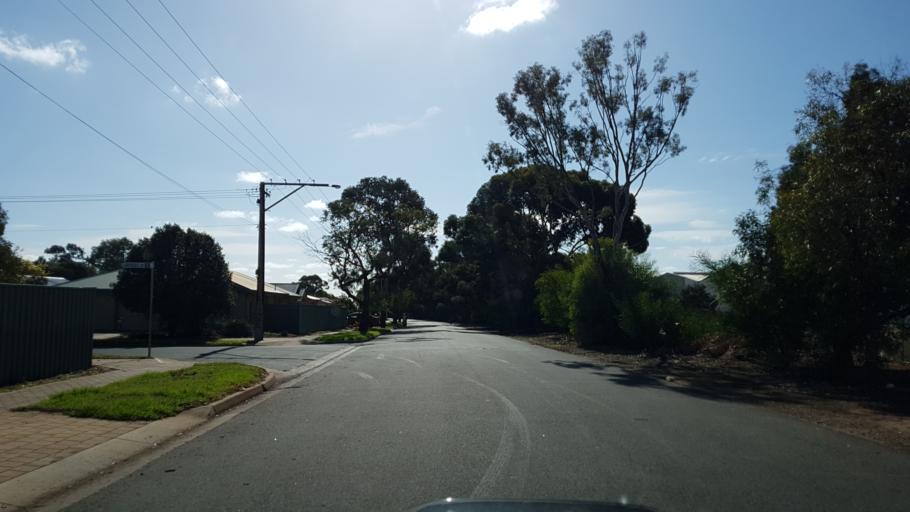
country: AU
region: South Australia
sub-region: Salisbury
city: Salisbury
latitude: -34.7520
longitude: 138.6407
